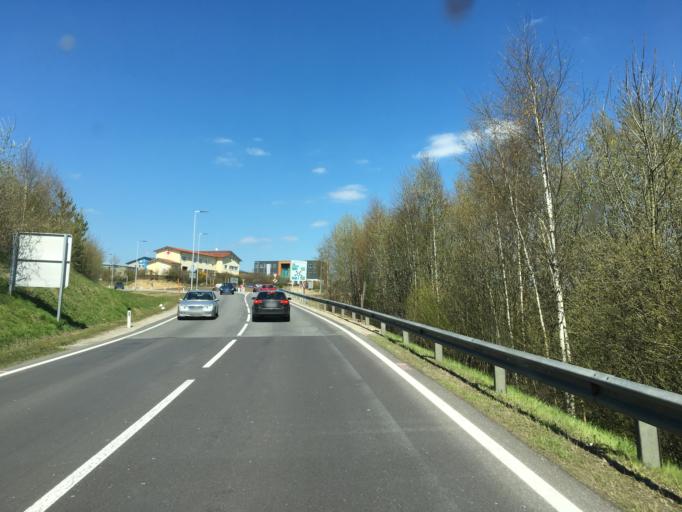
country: AT
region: Upper Austria
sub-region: Politischer Bezirk Urfahr-Umgebung
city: Bad Leonfelden
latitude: 48.5217
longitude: 14.3055
